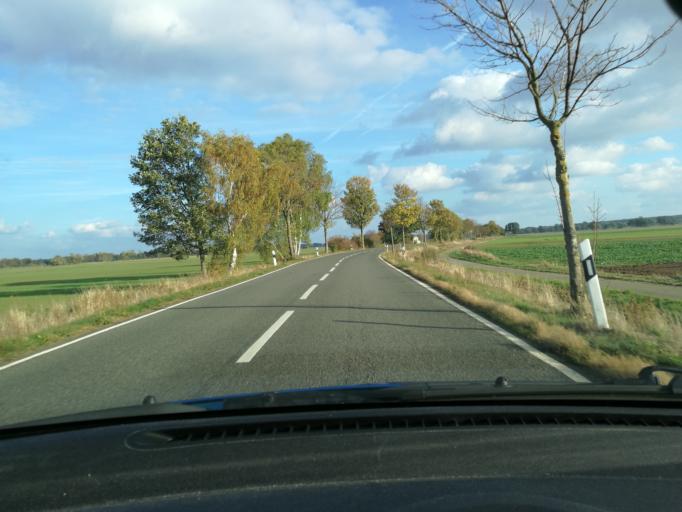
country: DE
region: Lower Saxony
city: Prezelle
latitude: 52.9060
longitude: 11.4137
